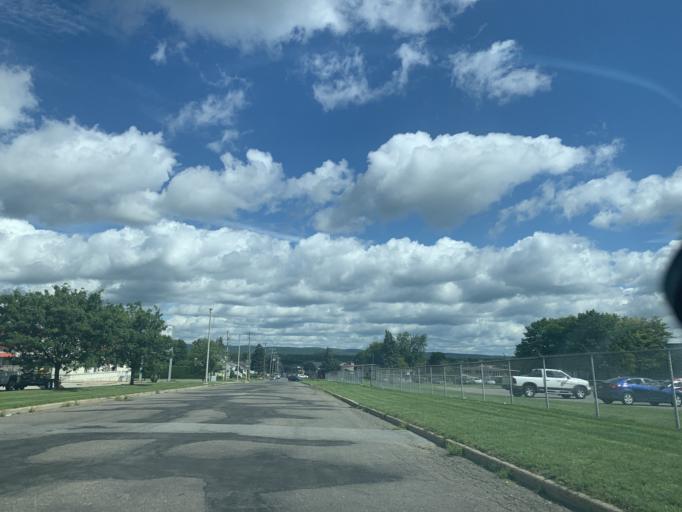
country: CA
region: Ontario
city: Hawkesbury
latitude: 45.6042
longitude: -74.5974
